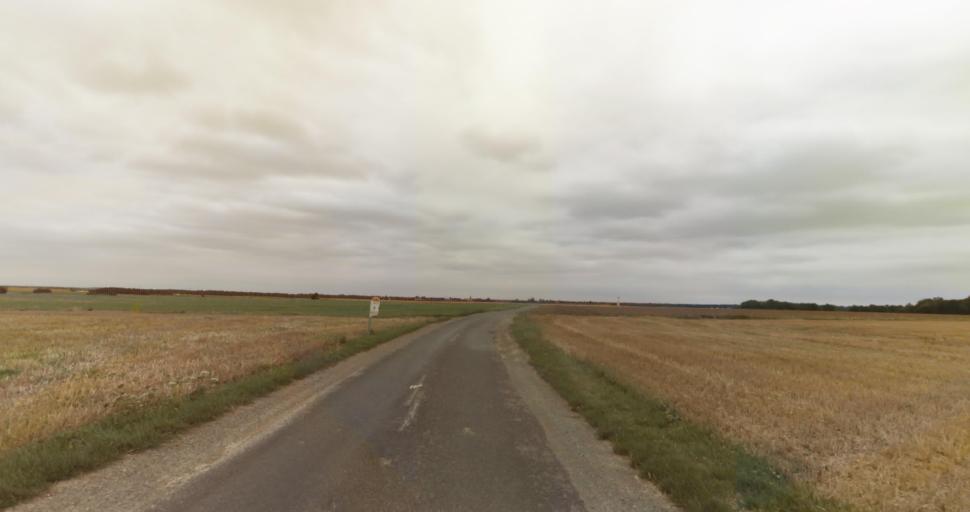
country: FR
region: Haute-Normandie
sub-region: Departement de l'Eure
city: La Couture-Boussey
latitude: 48.9212
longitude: 1.3329
